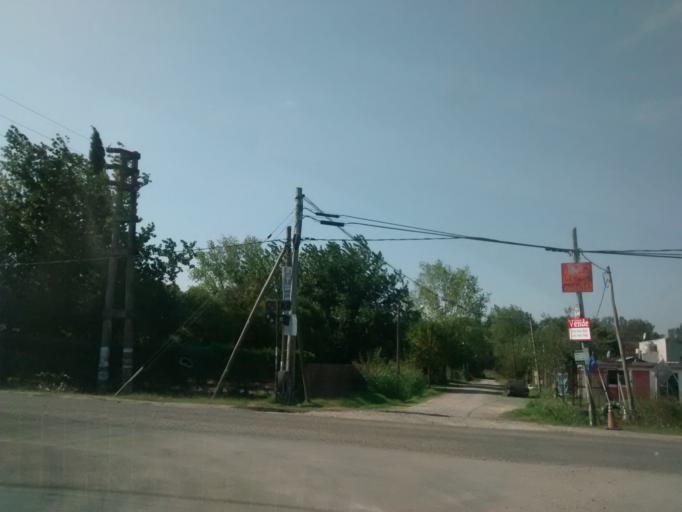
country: AR
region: Buenos Aires
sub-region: Partido de La Plata
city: La Plata
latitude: -34.9757
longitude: -57.8689
